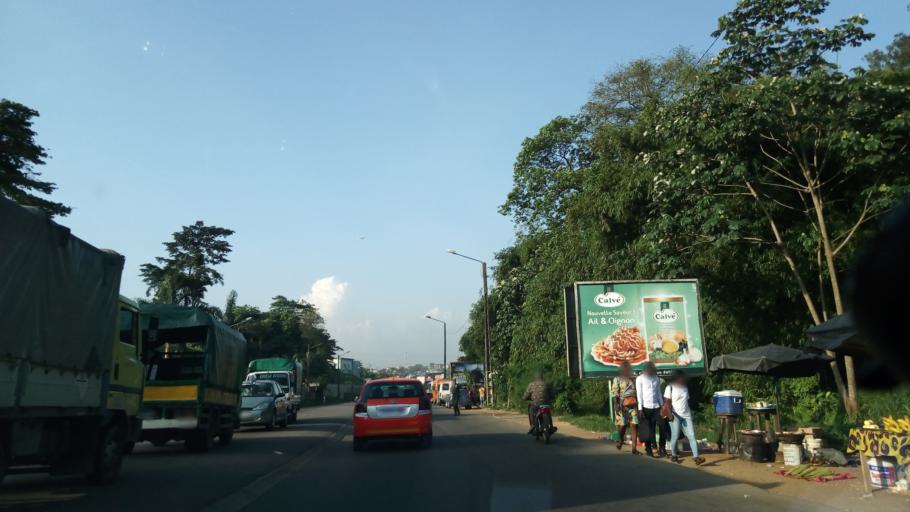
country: CI
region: Lagunes
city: Abobo
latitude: 5.3793
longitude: -4.0068
